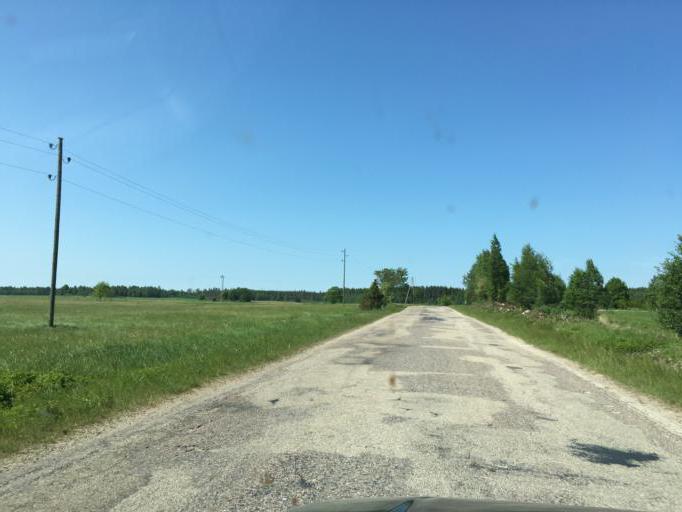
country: LV
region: Dundaga
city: Dundaga
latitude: 57.4684
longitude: 22.3223
